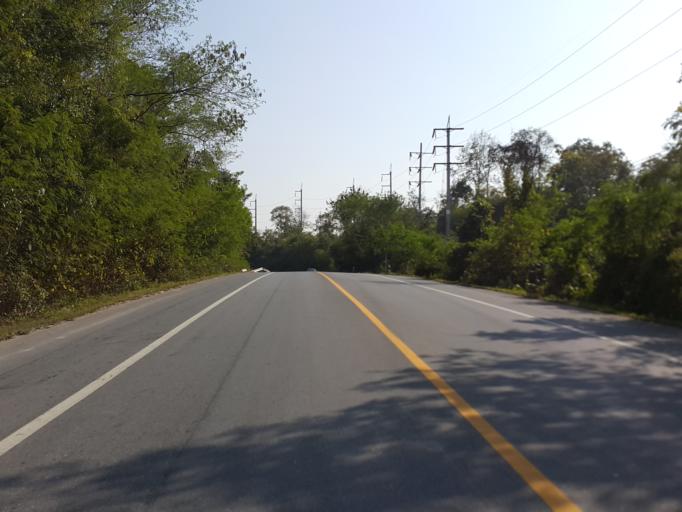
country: TH
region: Lampang
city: Chae Hom
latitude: 18.6129
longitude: 99.5397
